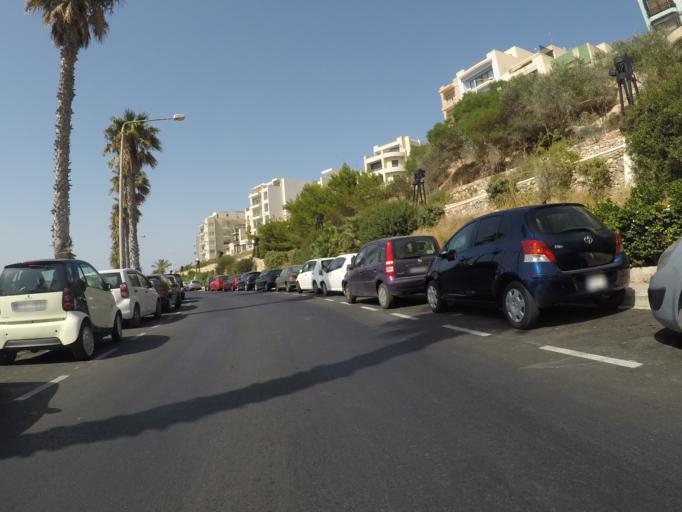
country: MT
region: Saint Paul's Bay
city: San Pawl il-Bahar
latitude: 35.9502
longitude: 14.4087
